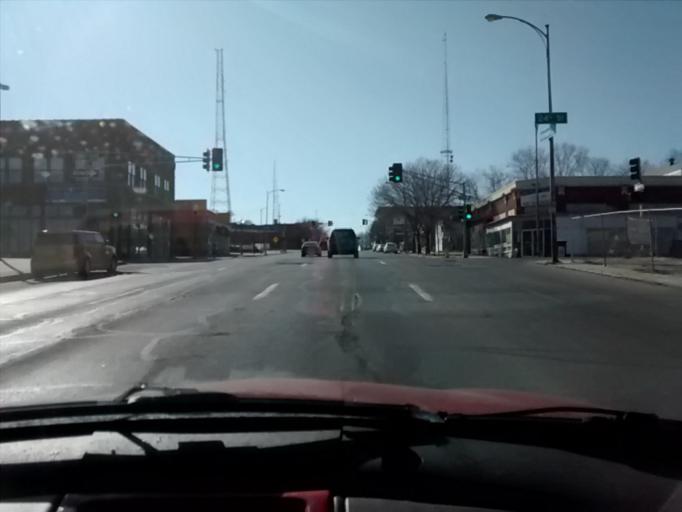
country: US
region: Nebraska
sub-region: Douglas County
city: Omaha
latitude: 41.2577
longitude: -95.9464
